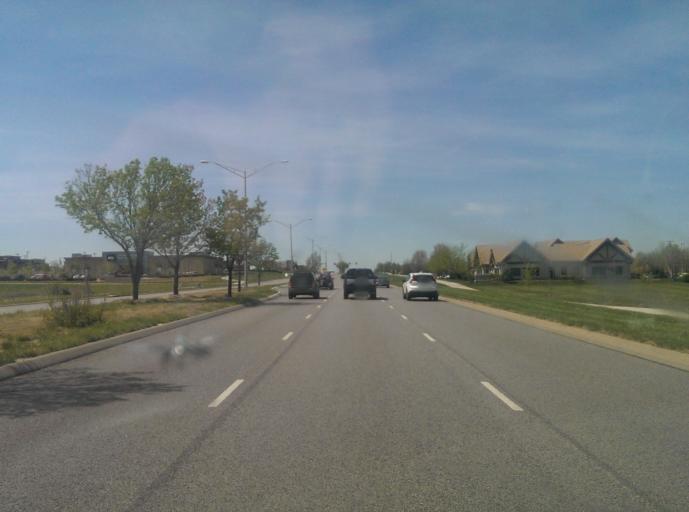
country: US
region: Kansas
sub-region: Johnson County
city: Leawood
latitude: 38.8839
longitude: -94.6548
